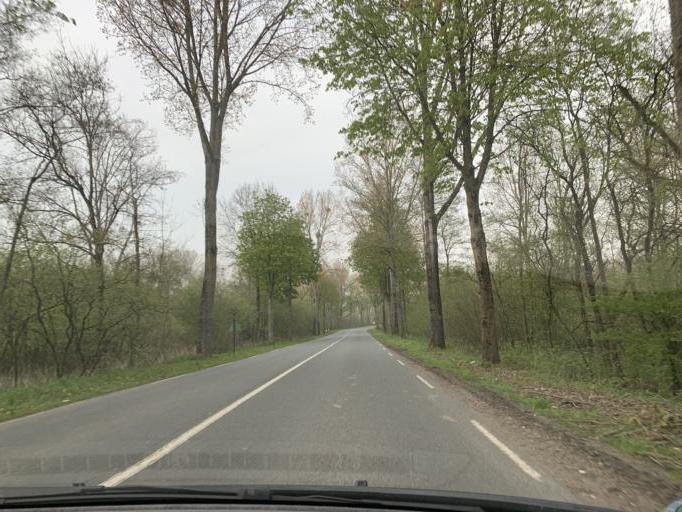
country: FR
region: Nord-Pas-de-Calais
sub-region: Departement du Pas-de-Calais
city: Montreuil
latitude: 50.4794
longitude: 1.7696
